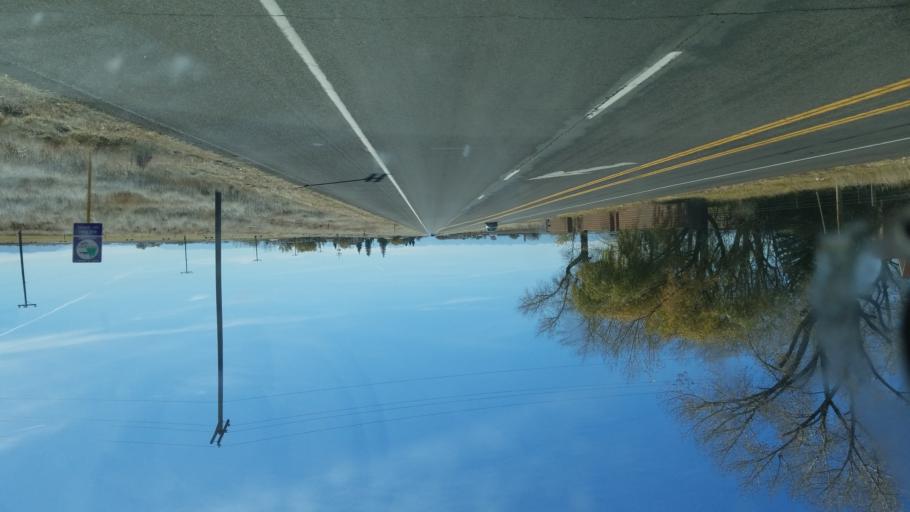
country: US
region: Colorado
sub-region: Rio Grande County
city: Monte Vista
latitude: 37.5587
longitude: -106.0918
